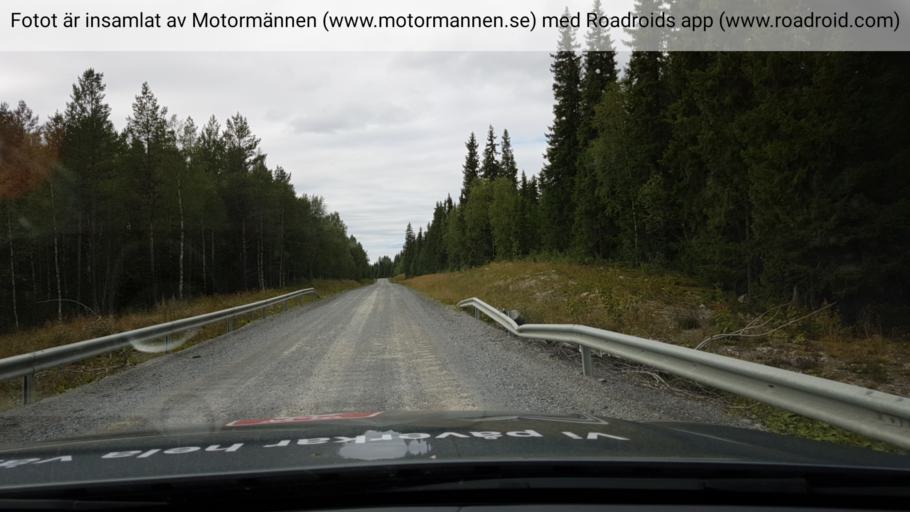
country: SE
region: Jaemtland
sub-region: Krokoms Kommun
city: Valla
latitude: 63.6472
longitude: 13.8188
